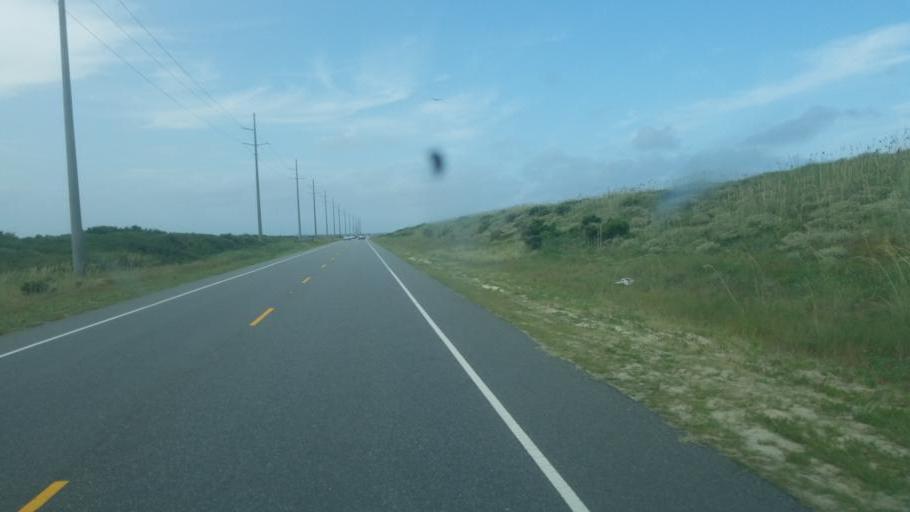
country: US
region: North Carolina
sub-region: Dare County
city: Buxton
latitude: 35.2835
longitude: -75.5165
